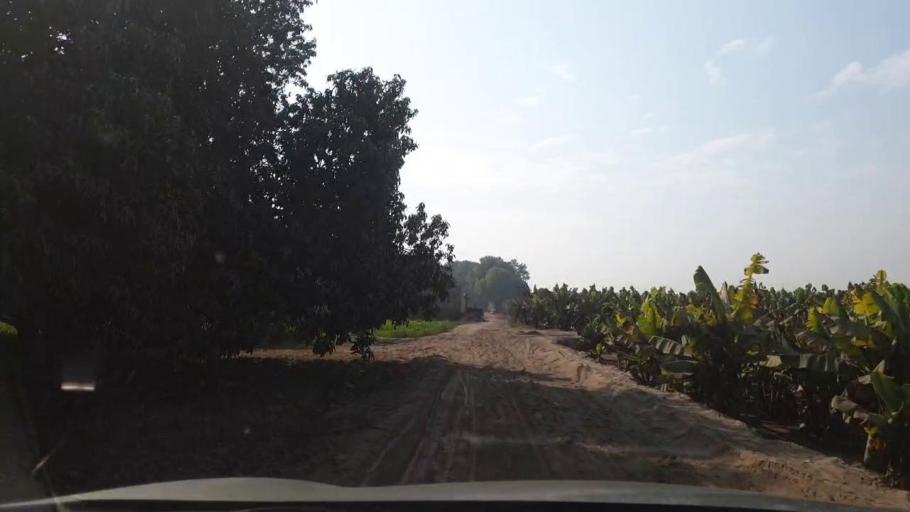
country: PK
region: Sindh
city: Tando Jam
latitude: 25.4687
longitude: 68.6193
